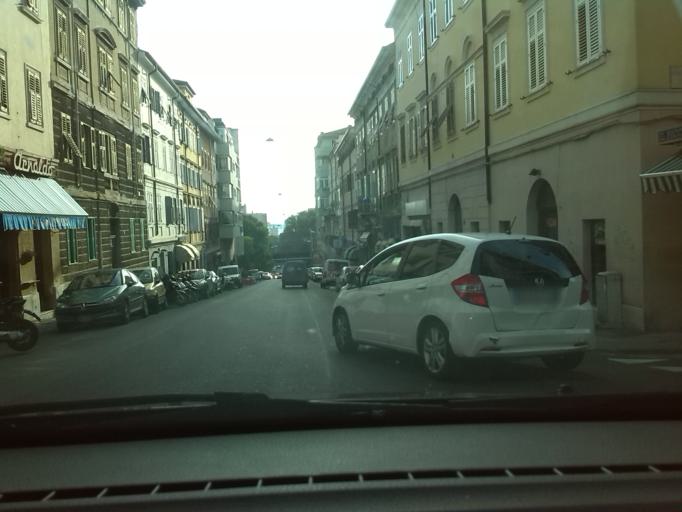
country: IT
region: Friuli Venezia Giulia
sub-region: Provincia di Trieste
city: Trieste
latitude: 45.6420
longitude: 13.7768
